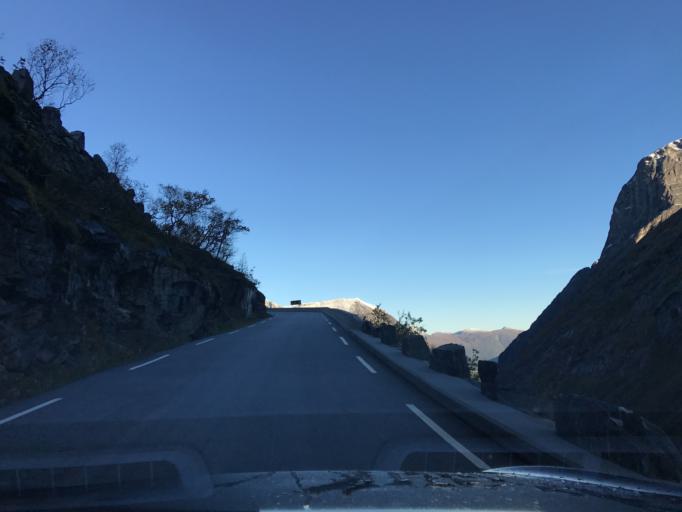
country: NO
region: More og Romsdal
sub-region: Rauma
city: Andalsnes
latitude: 62.4592
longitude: 7.6710
